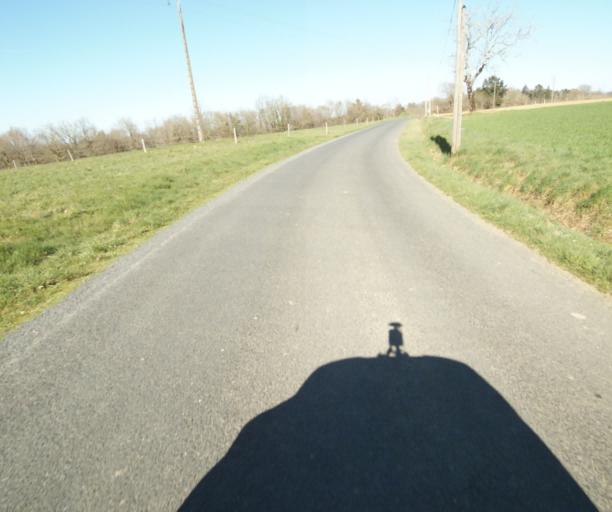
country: FR
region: Limousin
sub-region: Departement de la Correze
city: Chamboulive
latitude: 45.4278
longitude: 1.6473
